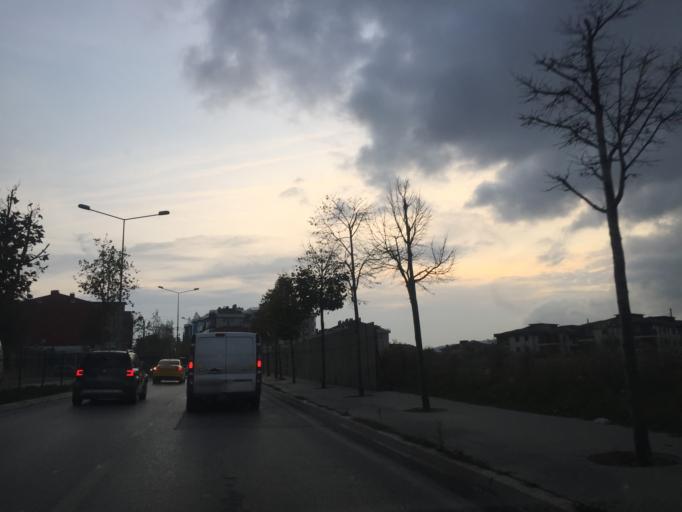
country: TR
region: Istanbul
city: Samandira
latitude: 40.9860
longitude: 29.2236
